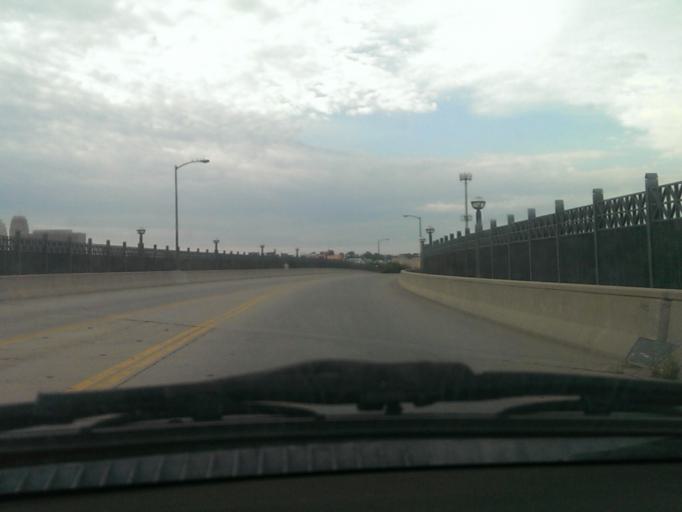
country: US
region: Missouri
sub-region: Jackson County
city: Kansas City
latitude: 39.0849
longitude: -94.5706
